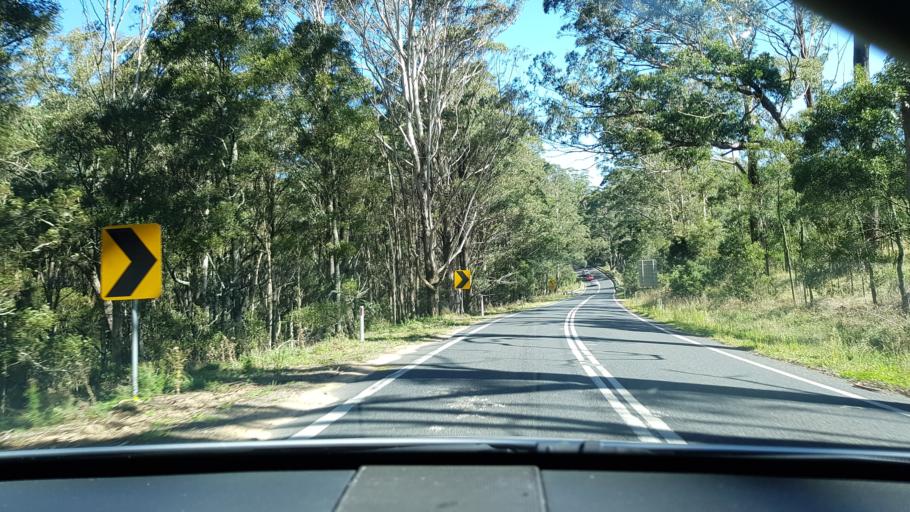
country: AU
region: New South Wales
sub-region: Lithgow
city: Bowenfels
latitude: -33.6702
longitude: 150.0519
